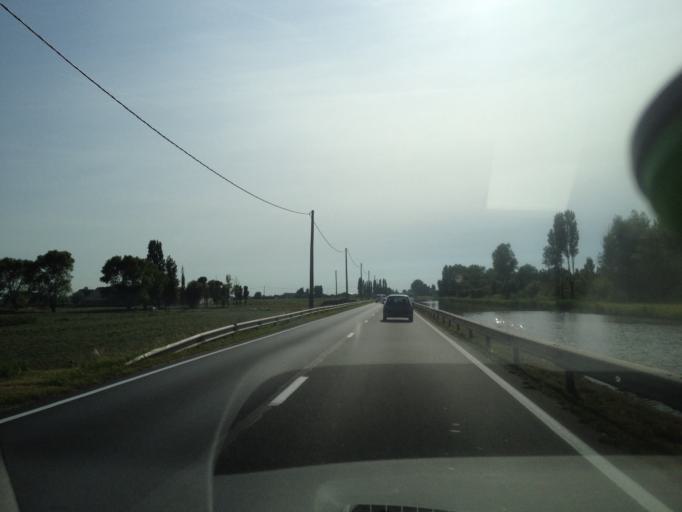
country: BE
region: Flanders
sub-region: Provincie West-Vlaanderen
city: Ostend
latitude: 51.1772
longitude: 2.9299
